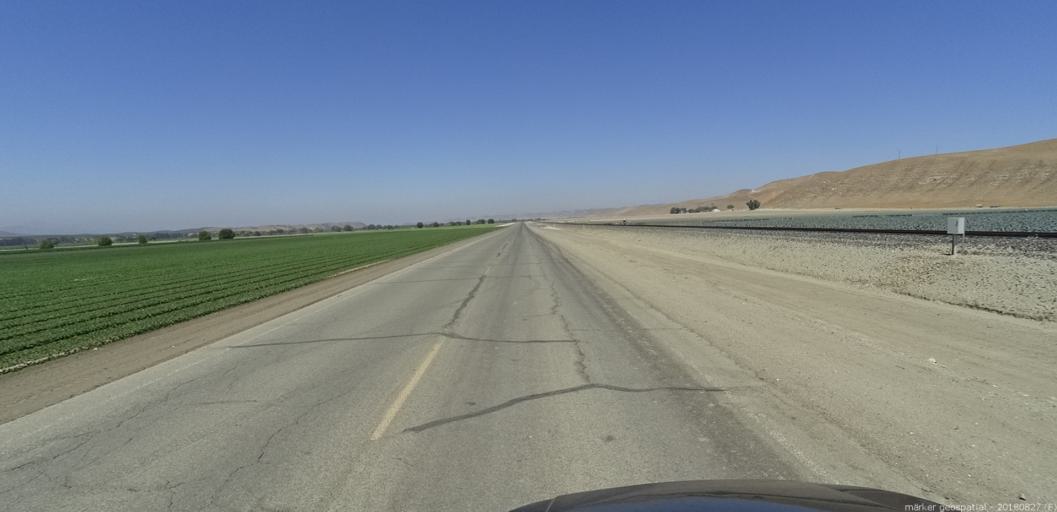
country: US
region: California
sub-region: Monterey County
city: King City
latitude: 36.0360
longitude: -120.9114
